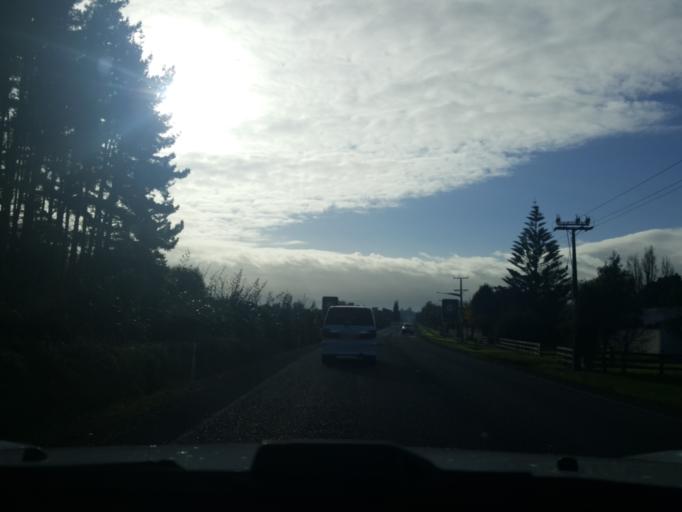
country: NZ
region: Waikato
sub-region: Waipa District
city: Cambridge
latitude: -37.6654
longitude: 175.5070
